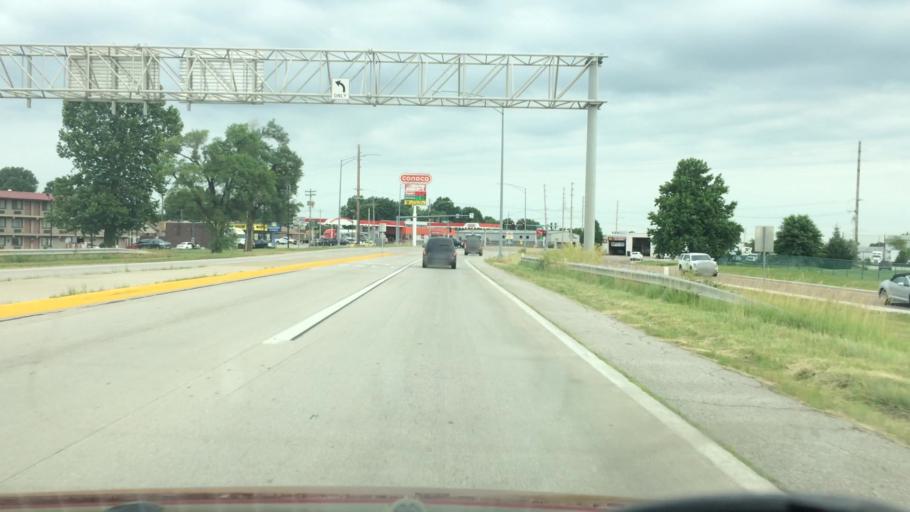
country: US
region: Missouri
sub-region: Greene County
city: Springfield
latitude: 37.2527
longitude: -93.2640
